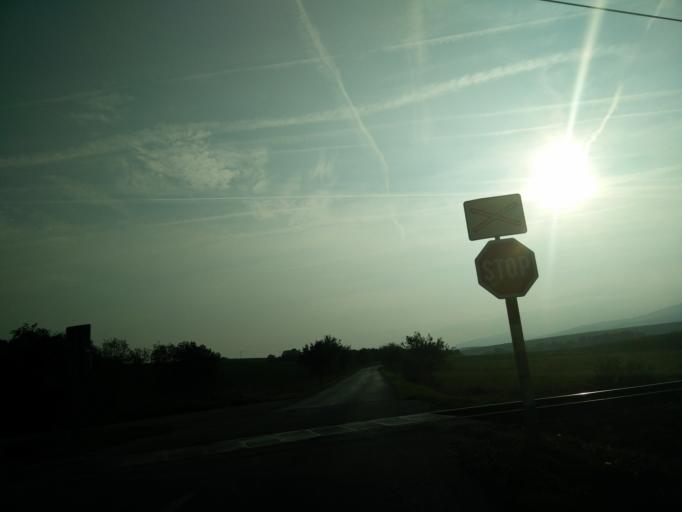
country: SK
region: Nitriansky
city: Banovce nad Bebravou
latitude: 48.7855
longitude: 18.1587
